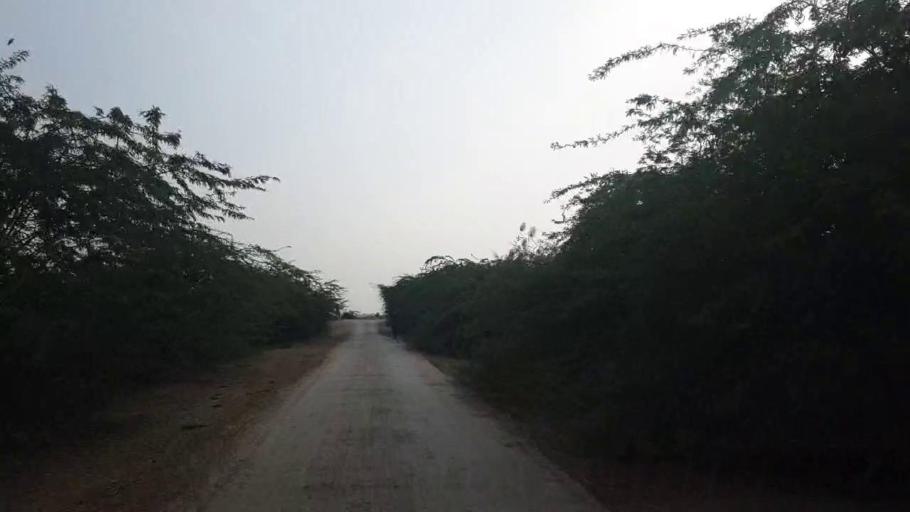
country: PK
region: Sindh
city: Badin
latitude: 24.6525
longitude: 68.7001
